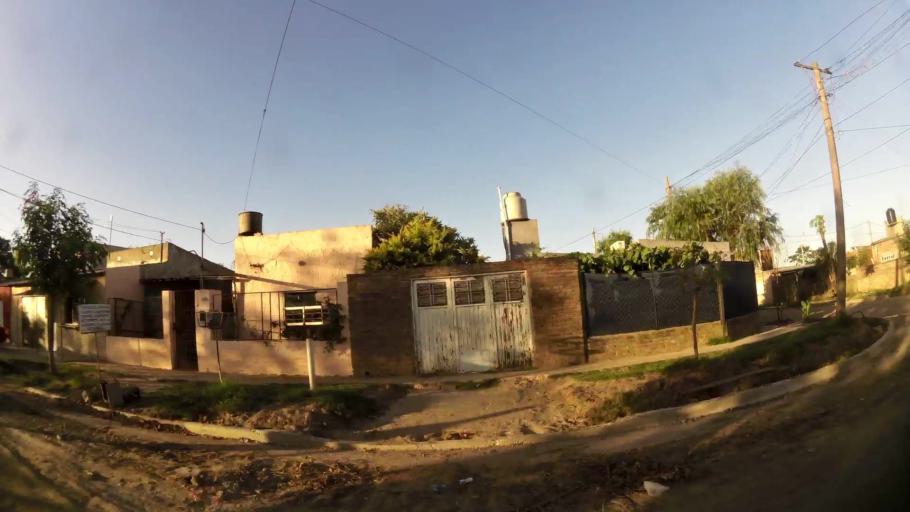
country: AR
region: Santa Fe
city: Santa Fe de la Vera Cruz
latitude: -31.5956
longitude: -60.6868
